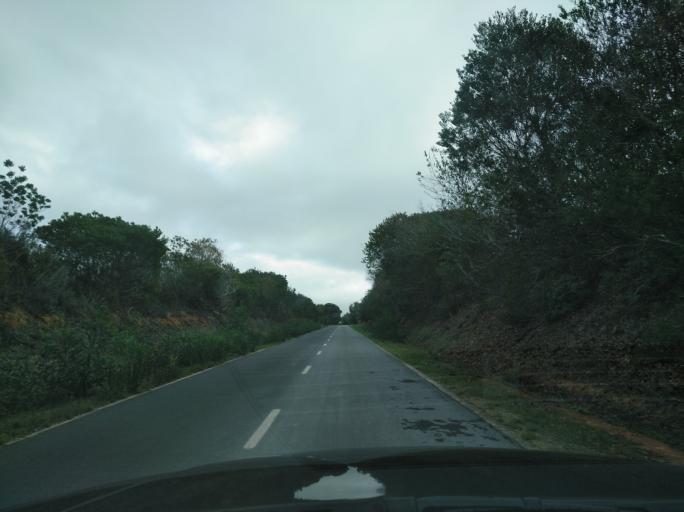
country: PT
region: Beja
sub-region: Odemira
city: Vila Nova de Milfontes
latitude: 37.7170
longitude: -8.7816
